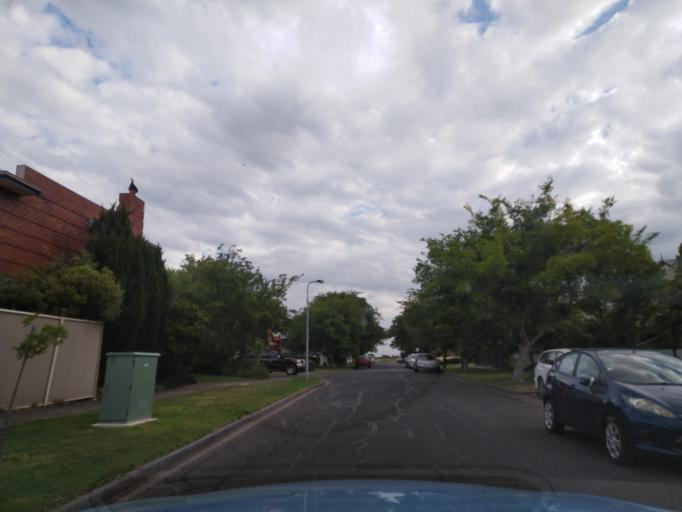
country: AU
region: Victoria
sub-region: Hobsons Bay
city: Williamstown North
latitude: -37.8627
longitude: 144.8821
